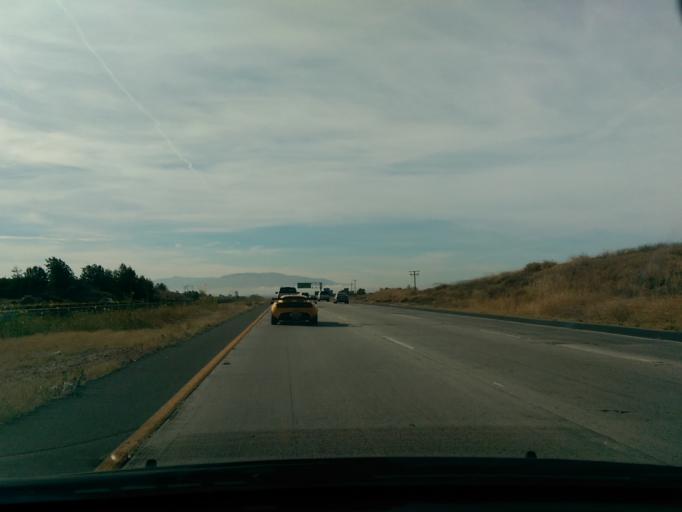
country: US
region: California
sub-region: Riverside County
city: Murrieta
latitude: 33.5724
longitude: -117.2164
